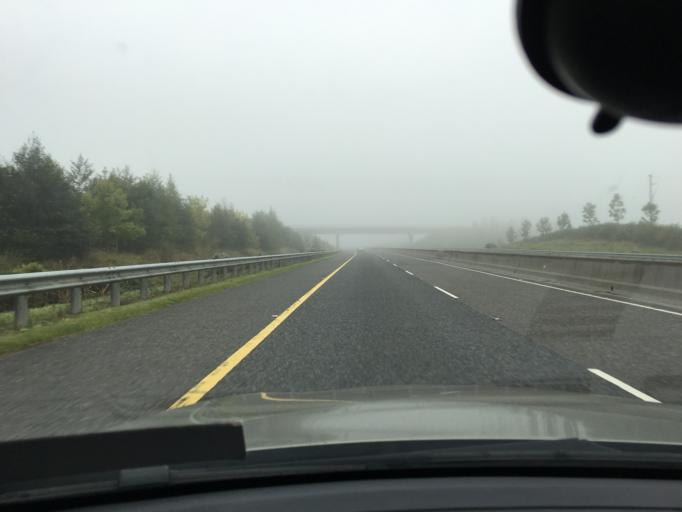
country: IE
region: Leinster
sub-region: Uibh Fhaili
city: Clara
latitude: 53.3887
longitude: -7.6061
